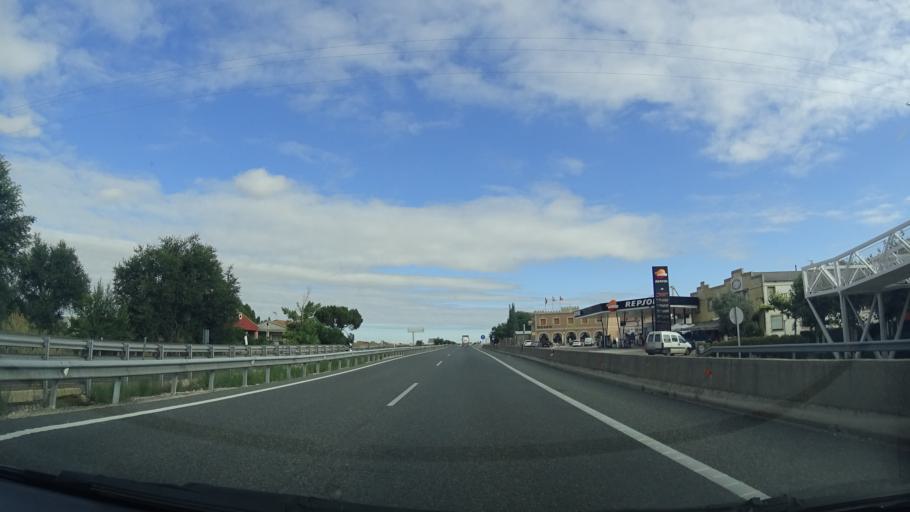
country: ES
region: Castille and Leon
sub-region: Provincia de Valladolid
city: Ataquines
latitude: 41.1809
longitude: -4.8073
